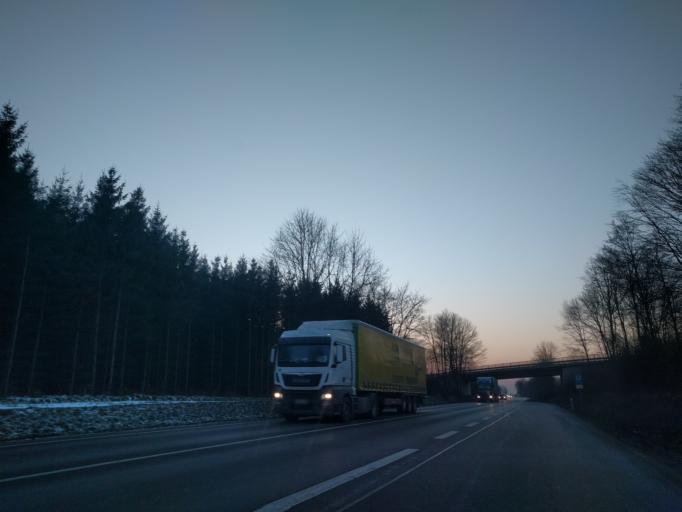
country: DE
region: Bavaria
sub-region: Swabia
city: Rain
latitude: 48.7030
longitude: 10.9080
